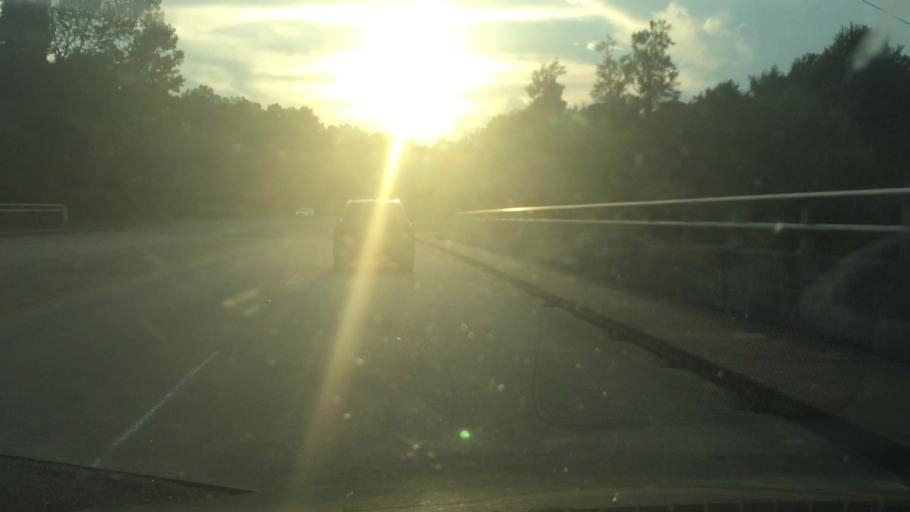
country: US
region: South Carolina
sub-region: Horry County
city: Forestbrook
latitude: 33.7302
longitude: -78.9444
